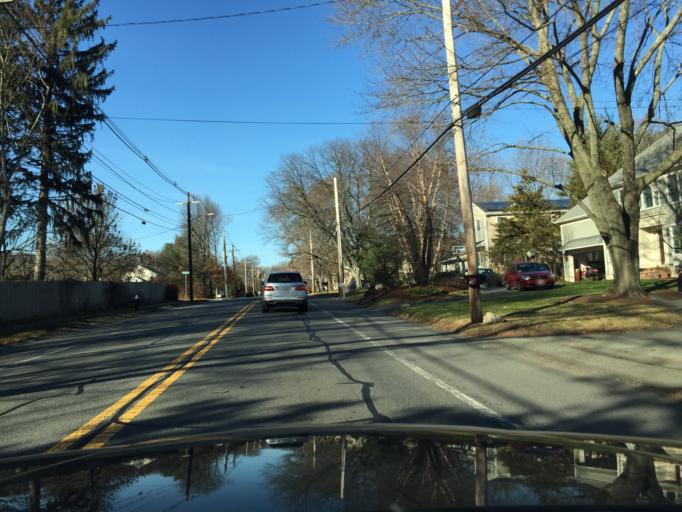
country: US
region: Massachusetts
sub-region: Middlesex County
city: Lexington
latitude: 42.4397
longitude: -71.1920
